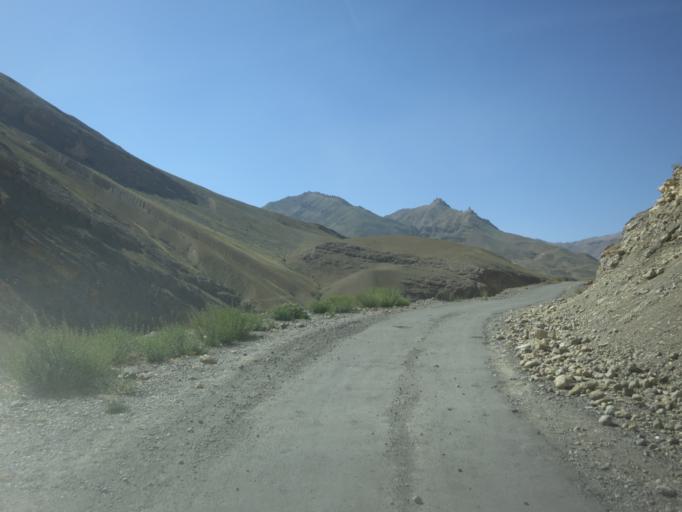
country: IN
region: Himachal Pradesh
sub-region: Kulu
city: Manali
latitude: 32.3184
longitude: 78.0020
